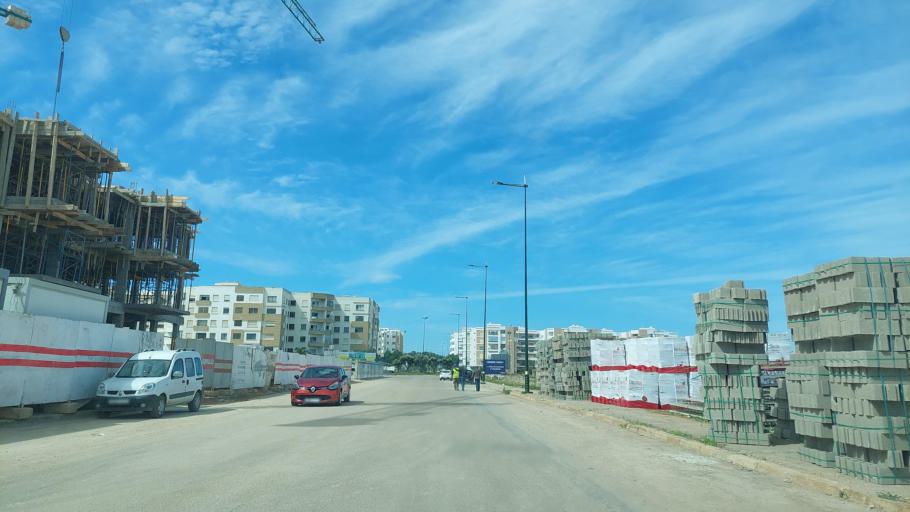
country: MA
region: Chaouia-Ouardigha
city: Nouaseur
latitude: 33.3928
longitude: -7.5602
